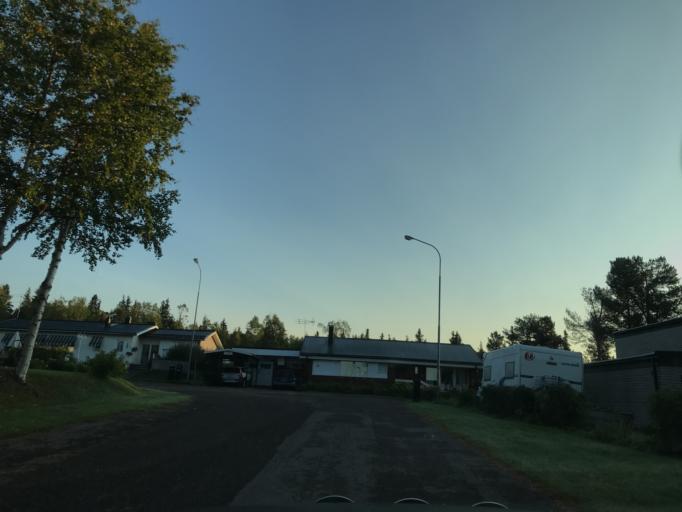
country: SE
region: Norrbotten
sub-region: Gallivare Kommun
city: Malmberget
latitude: 67.6515
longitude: 21.0491
